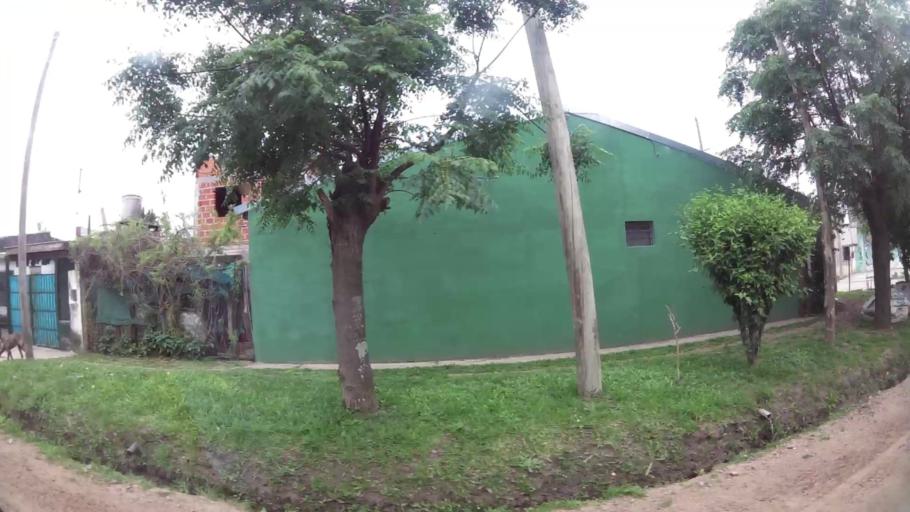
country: AR
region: Buenos Aires
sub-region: Partido de Campana
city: Campana
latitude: -34.2123
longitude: -58.9395
